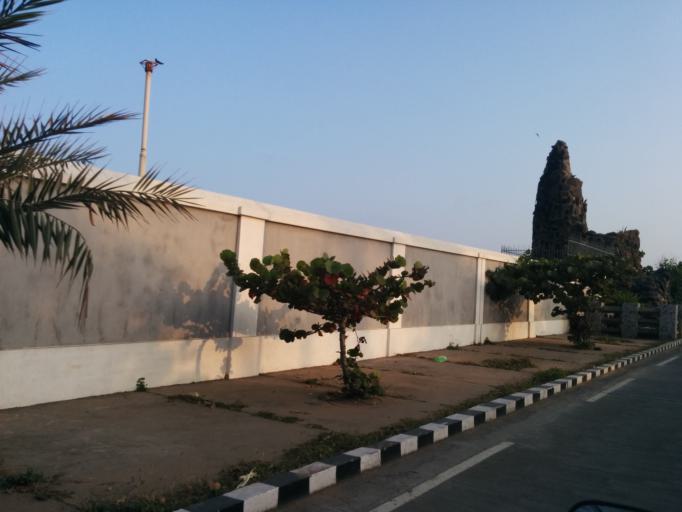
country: IN
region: Pondicherry
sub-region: Puducherry
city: Puducherry
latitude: 11.9372
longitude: 79.8363
